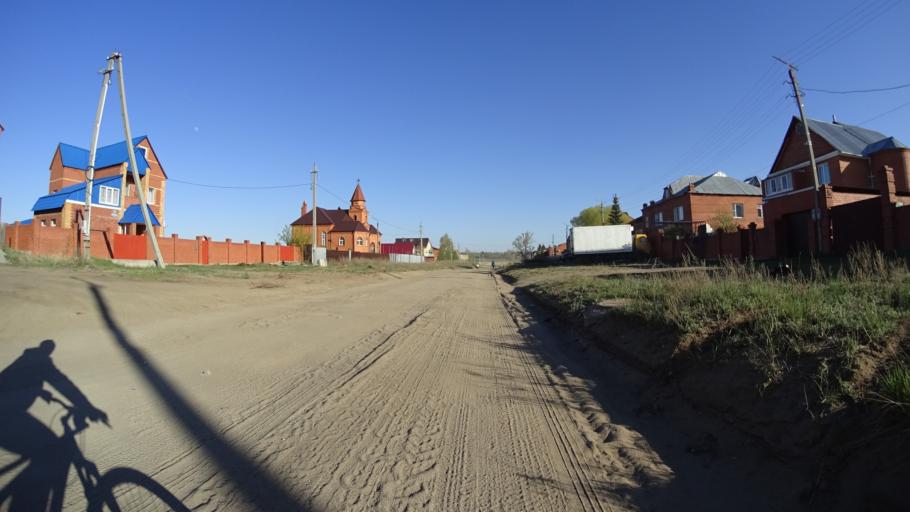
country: RU
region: Chelyabinsk
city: Troitsk
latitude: 54.0721
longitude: 61.5355
